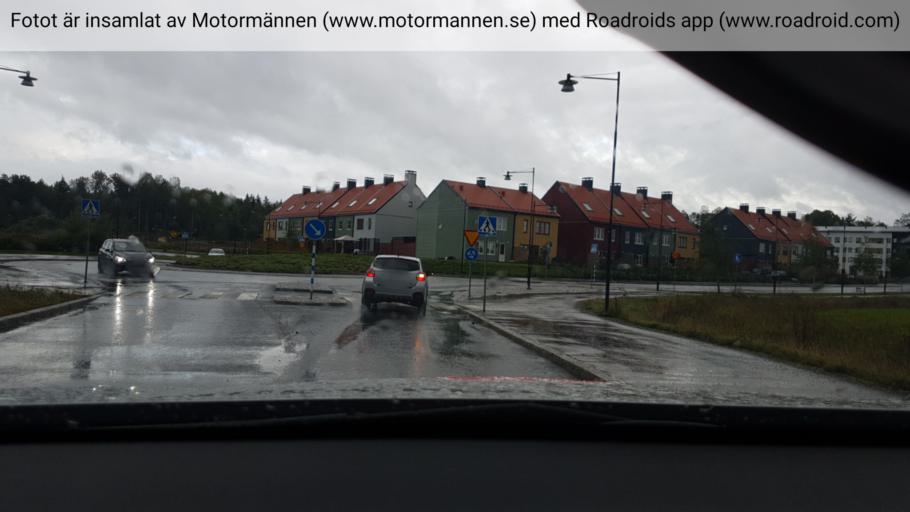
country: SE
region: Stockholm
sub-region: Haninge Kommun
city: Jordbro
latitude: 59.1016
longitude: 18.0487
